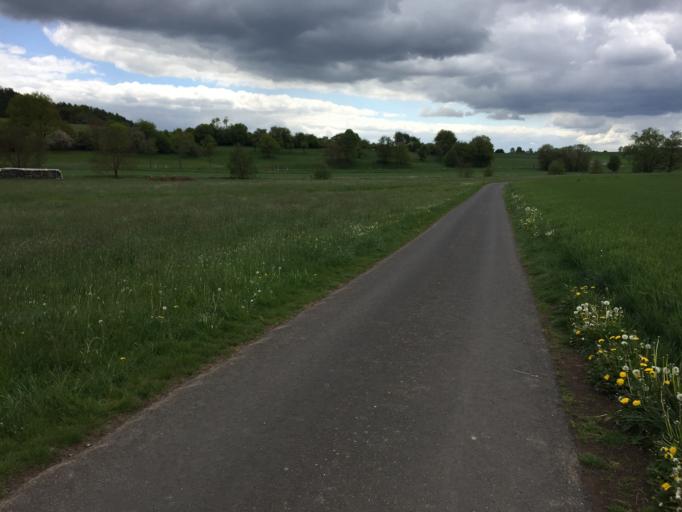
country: DE
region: Hesse
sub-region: Regierungsbezirk Giessen
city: Grunberg
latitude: 50.5737
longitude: 8.9215
